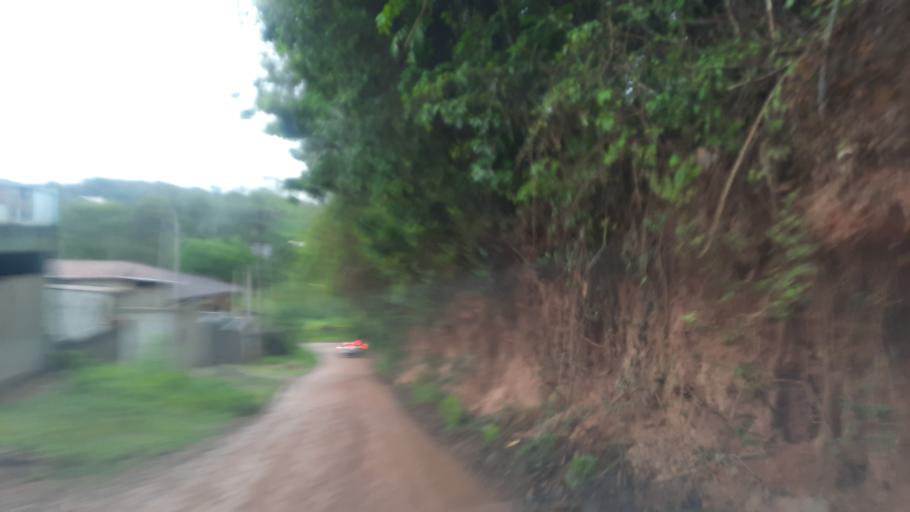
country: BR
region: Sao Paulo
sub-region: Atibaia
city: Atibaia
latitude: -23.0725
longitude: -46.5131
